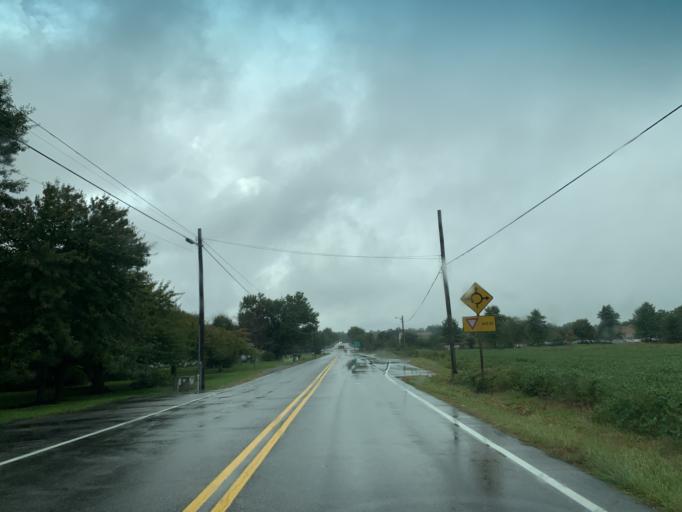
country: US
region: Maryland
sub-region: Queen Anne's County
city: Kingstown
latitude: 39.2631
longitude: -75.8590
